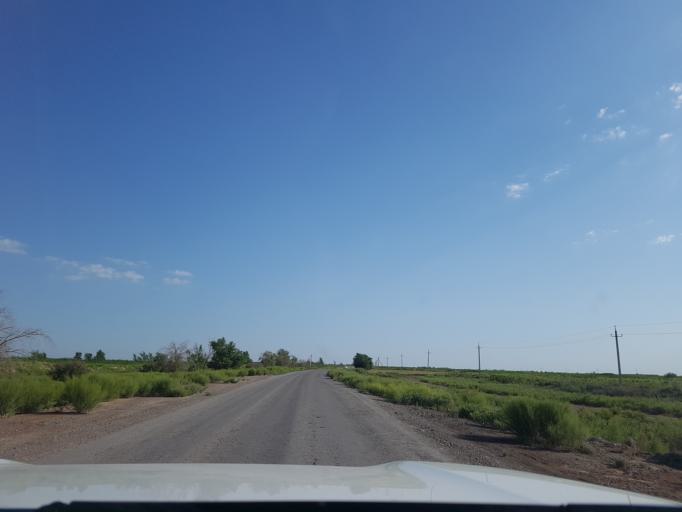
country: TM
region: Dasoguz
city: Koeneuergench
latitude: 41.8967
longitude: 58.7072
